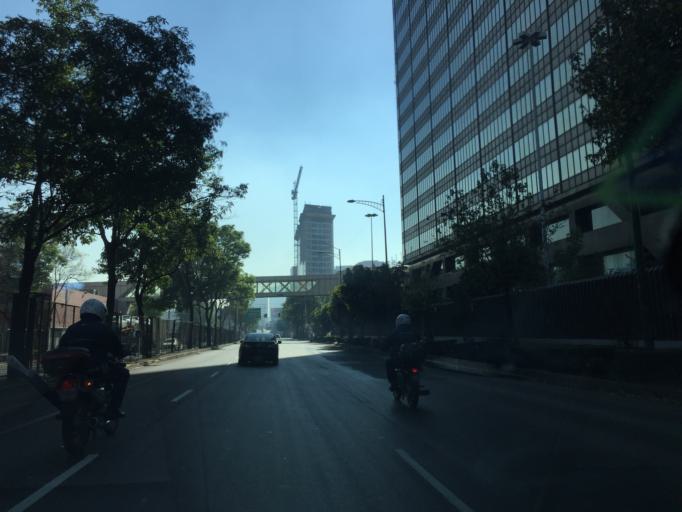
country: MX
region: Mexico City
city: Miguel Hidalgo
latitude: 19.4397
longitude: -99.1752
